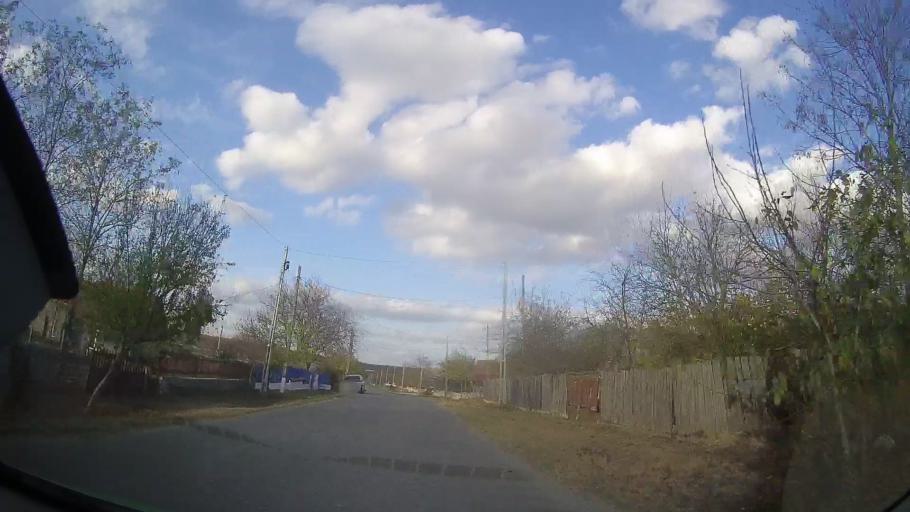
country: RO
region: Constanta
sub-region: Comuna Cerchezu
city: Cerchezu
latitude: 43.8532
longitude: 28.1010
